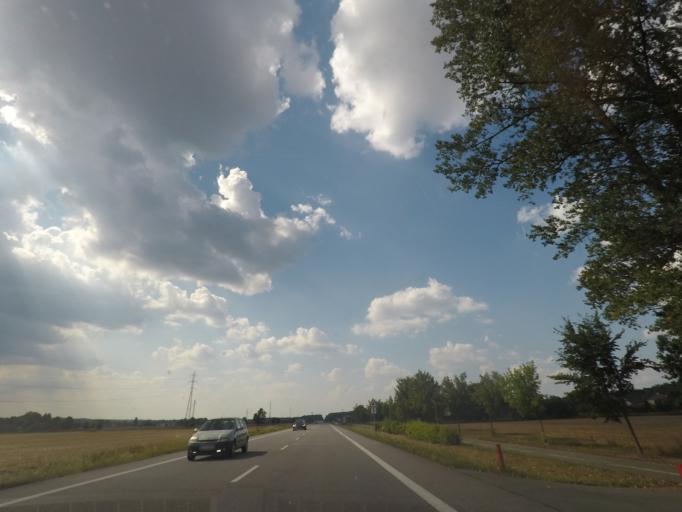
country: CZ
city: Albrechtice nad Orlici
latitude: 50.1659
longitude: 16.0486
